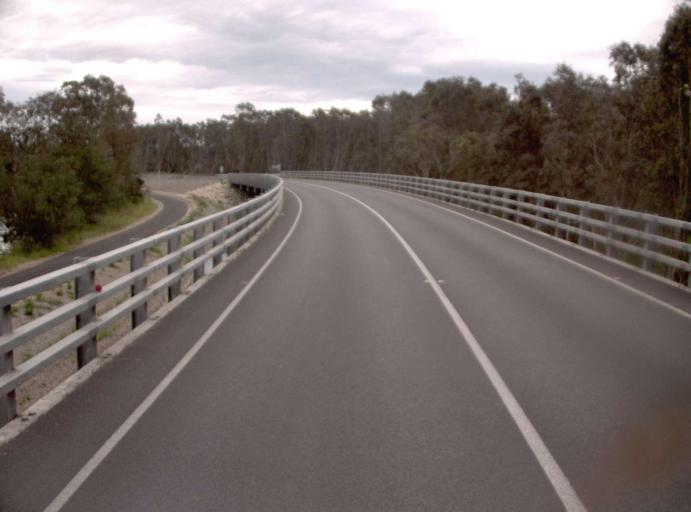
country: AU
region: Victoria
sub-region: Wellington
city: Sale
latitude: -38.1348
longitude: 147.0769
